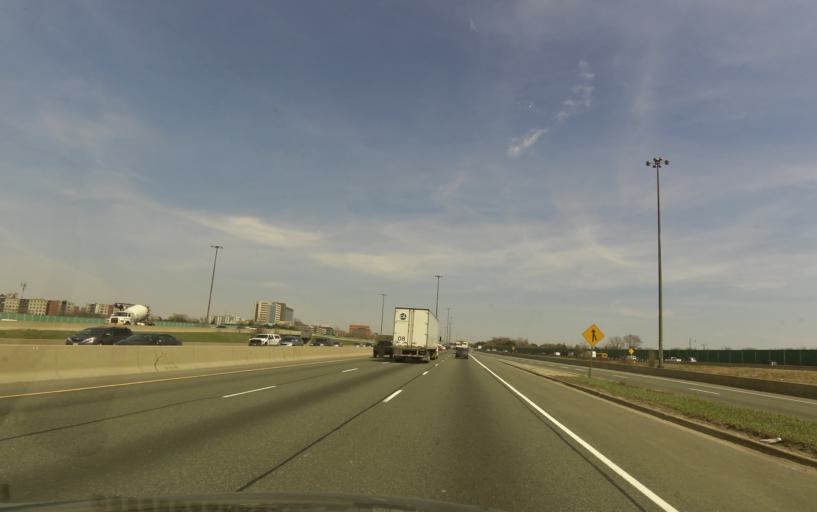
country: CA
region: Ontario
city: Concord
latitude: 43.7184
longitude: -79.5005
